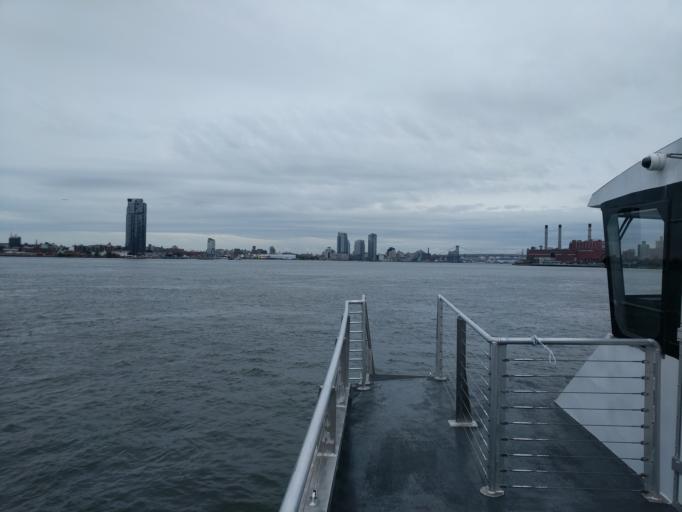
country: US
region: New York
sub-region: Queens County
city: Long Island City
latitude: 40.7413
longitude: -73.9699
